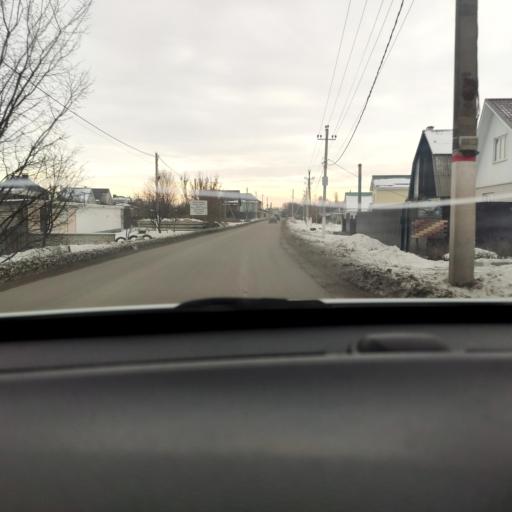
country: RU
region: Voronezj
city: Somovo
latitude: 51.6740
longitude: 39.3358
